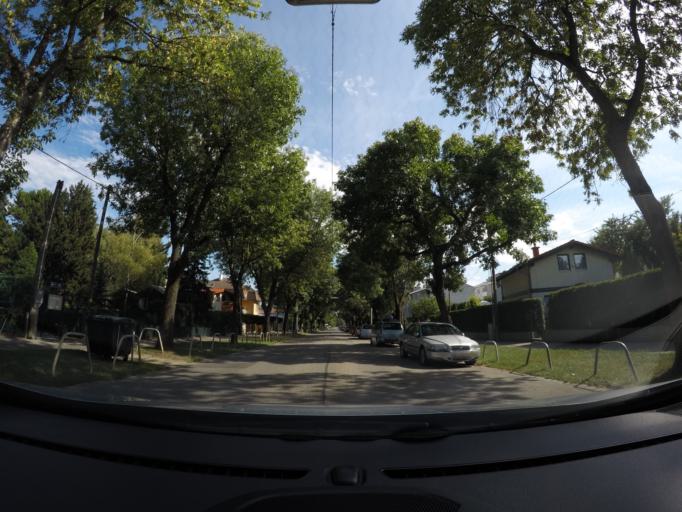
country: AT
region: Vienna
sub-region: Wien Stadt
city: Vienna
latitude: 48.2029
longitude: 16.2908
